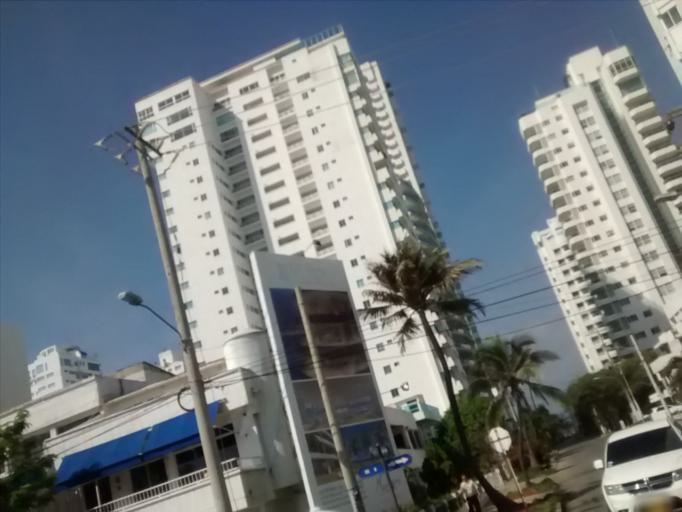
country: CO
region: Bolivar
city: Cartagena
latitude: 10.3974
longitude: -75.5542
